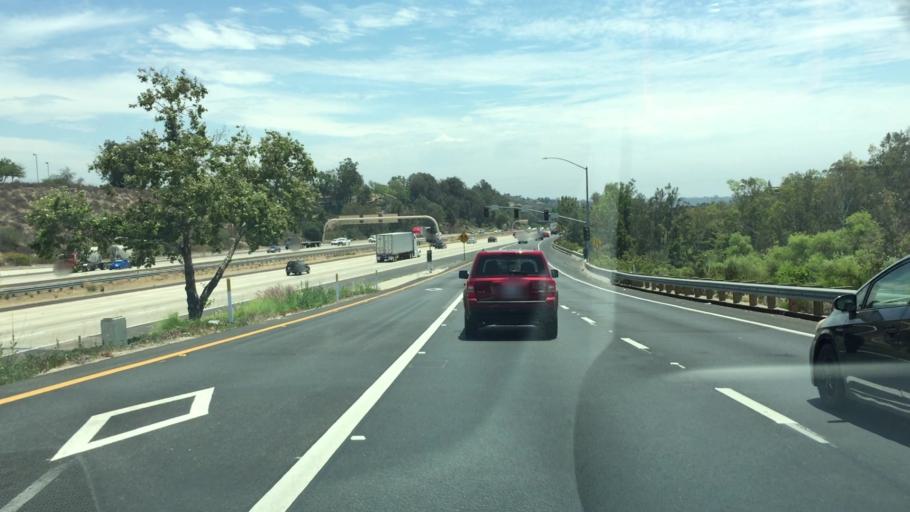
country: US
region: California
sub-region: San Diego County
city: La Mesa
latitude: 32.8325
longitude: -117.1192
